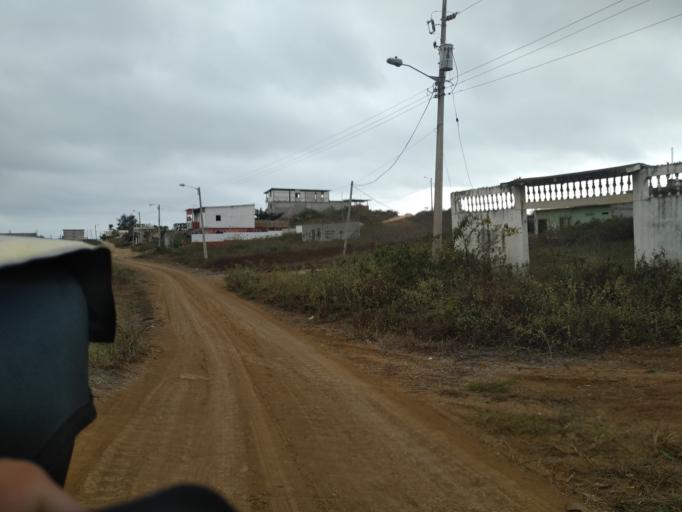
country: EC
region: Santa Elena
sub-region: Canton Santa Elena
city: Santa Elena
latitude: -2.2053
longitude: -80.8646
